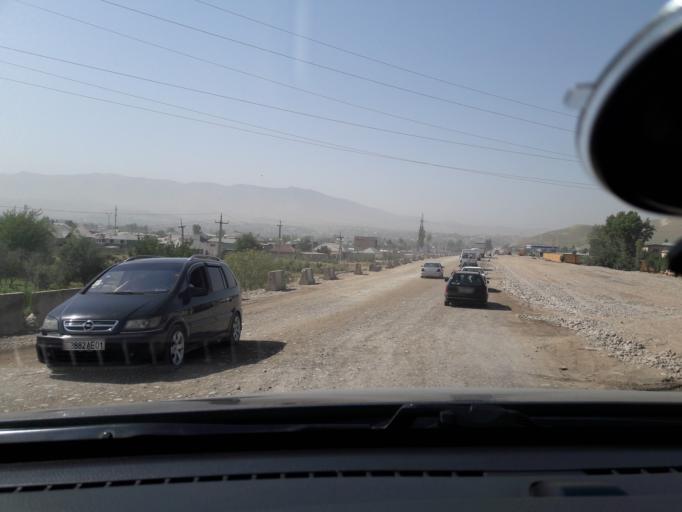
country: TJ
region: Dushanbe
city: Boshkengash
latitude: 38.4566
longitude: 68.7361
